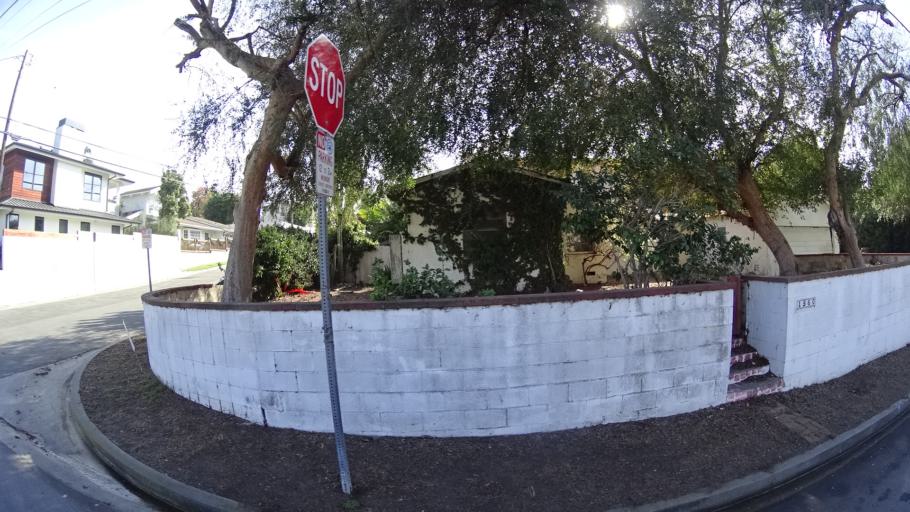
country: US
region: California
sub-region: Los Angeles County
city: Hermosa Beach
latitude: 33.8794
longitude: -118.3853
